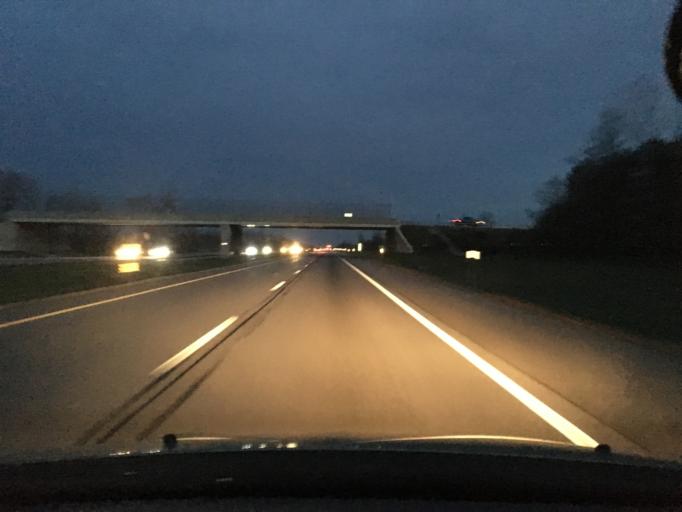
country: US
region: New York
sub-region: Ontario County
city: Victor
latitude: 42.9911
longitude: -77.3276
